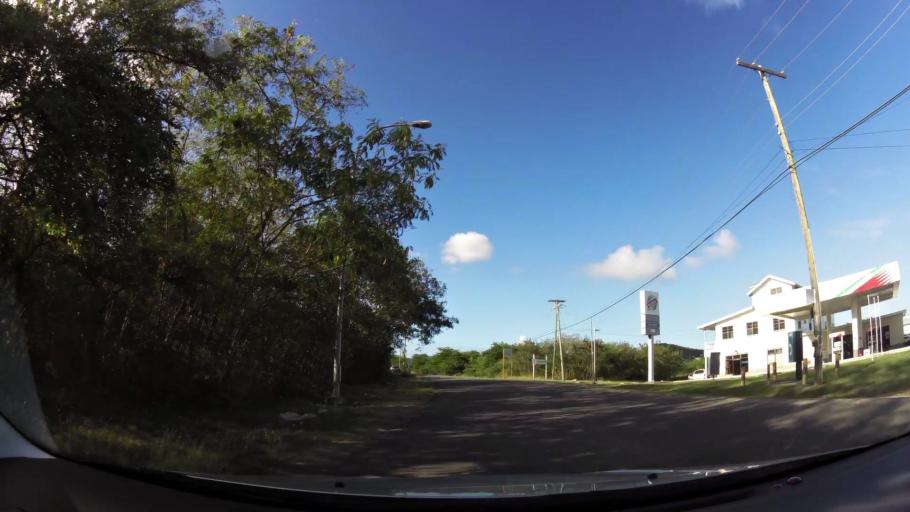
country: AG
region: Saint George
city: Piggotts
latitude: 17.1123
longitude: -61.8017
